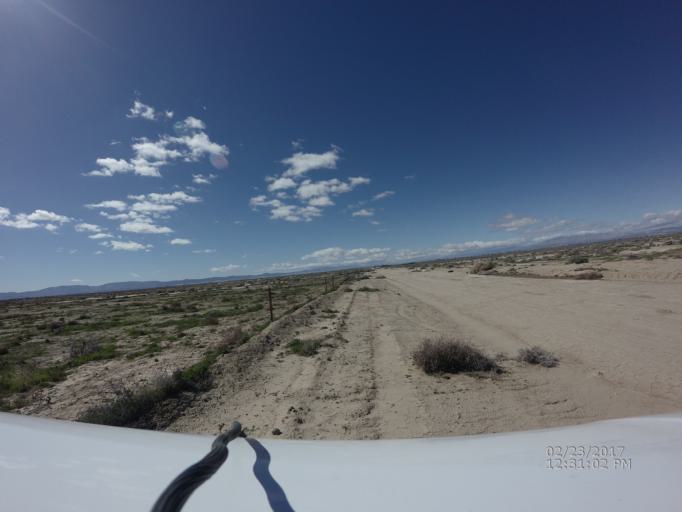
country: US
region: California
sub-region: Los Angeles County
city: Lancaster
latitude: 34.7483
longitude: -118.0513
